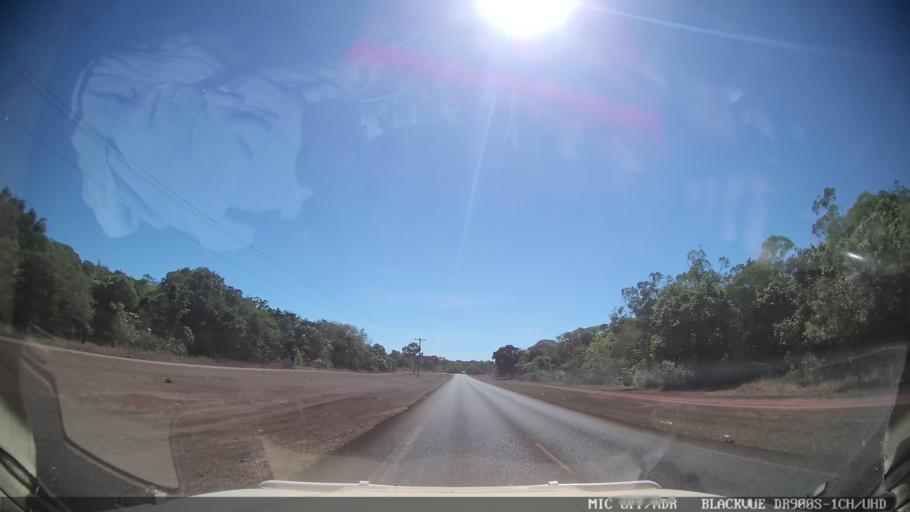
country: AU
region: Queensland
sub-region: Torres
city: Thursday Island
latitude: -10.8999
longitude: 142.3357
